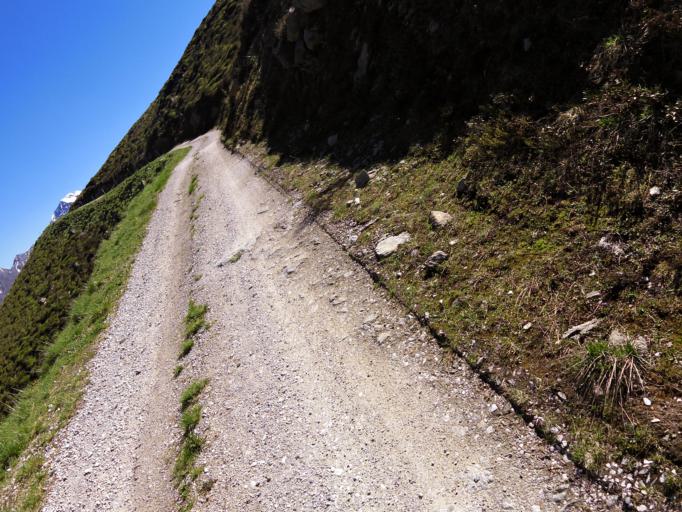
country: AT
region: Tyrol
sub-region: Politischer Bezirk Innsbruck Land
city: Neustift im Stubaital
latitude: 47.1262
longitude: 11.2810
